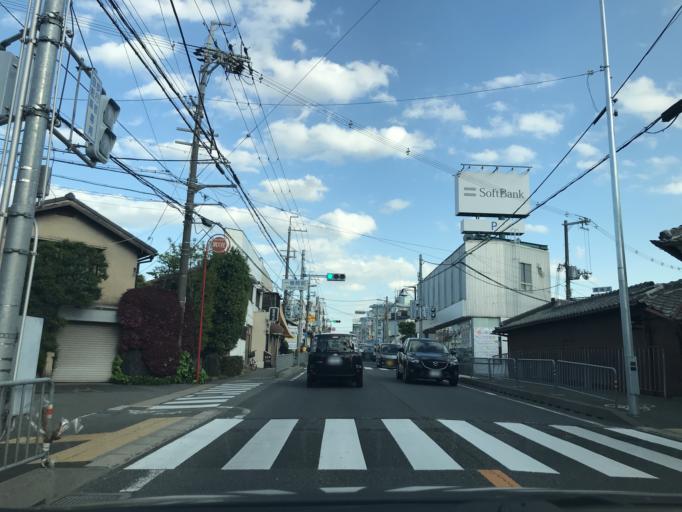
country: JP
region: Osaka
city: Ikeda
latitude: 34.8156
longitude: 135.4372
